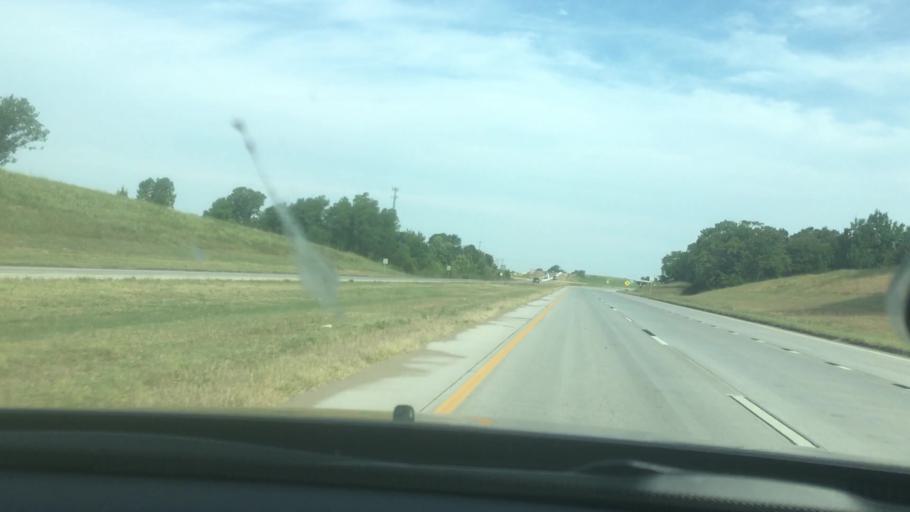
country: US
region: Oklahoma
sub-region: Pontotoc County
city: Ada
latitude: 34.7825
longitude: -96.7177
